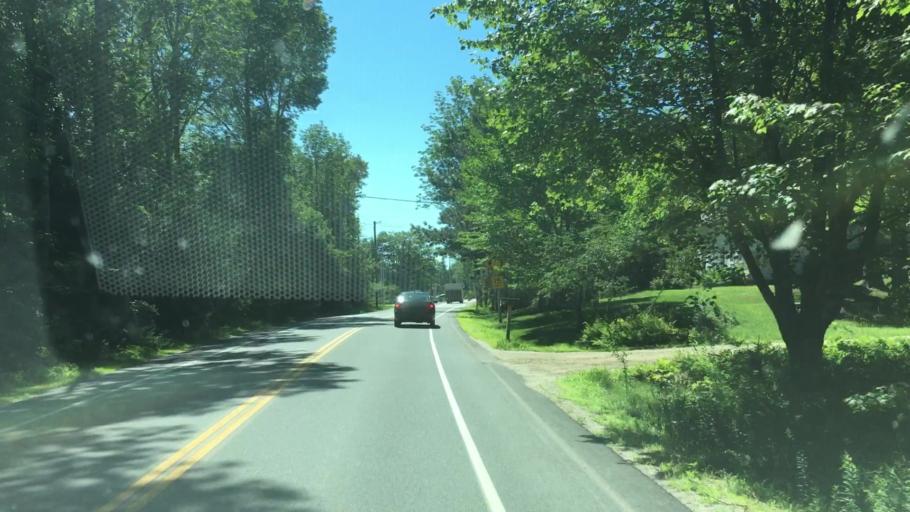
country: US
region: Maine
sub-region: Hancock County
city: Sedgwick
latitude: 44.4092
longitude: -68.5992
